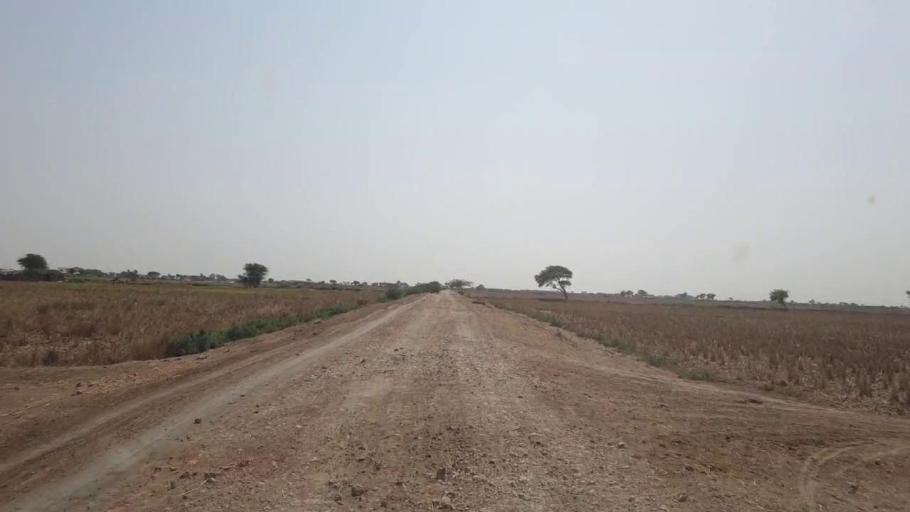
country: PK
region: Sindh
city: Jati
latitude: 24.4325
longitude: 68.5523
